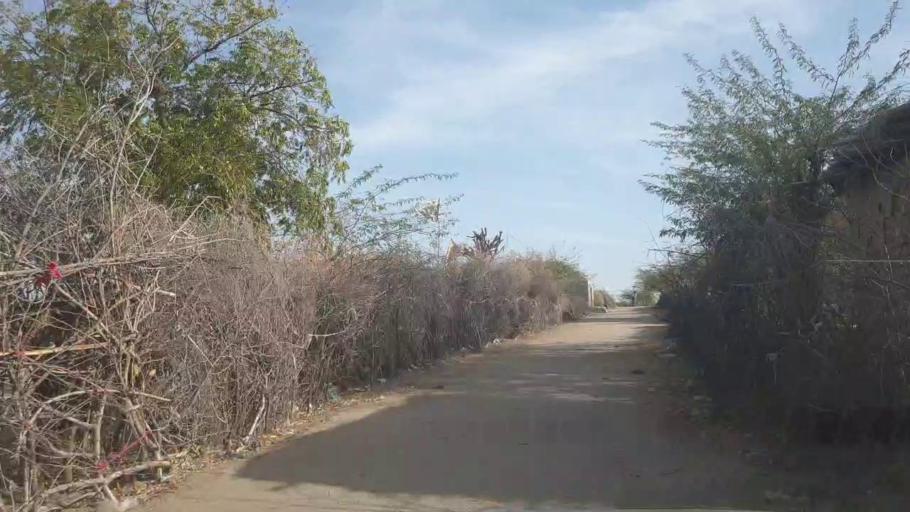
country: PK
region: Sindh
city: Nabisar
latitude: 25.0622
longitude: 69.6443
